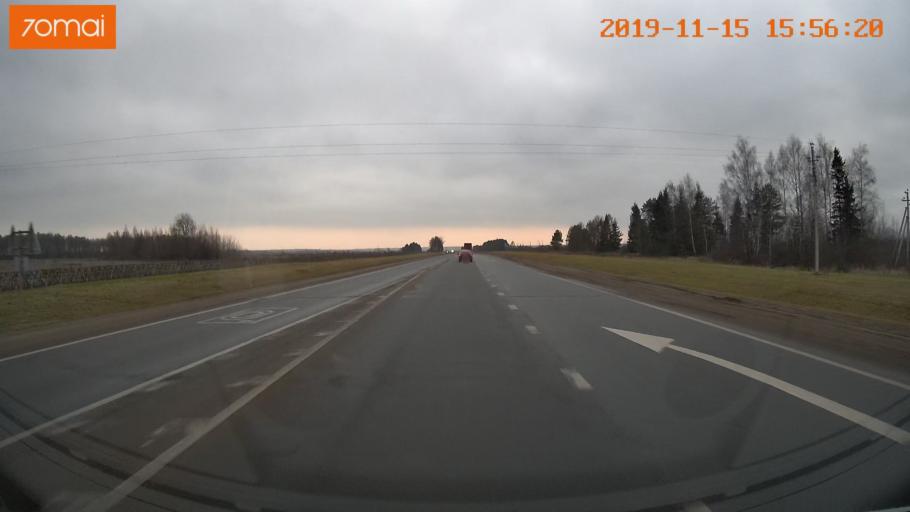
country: RU
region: Jaroslavl
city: Yaroslavl
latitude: 57.8433
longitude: 39.9747
